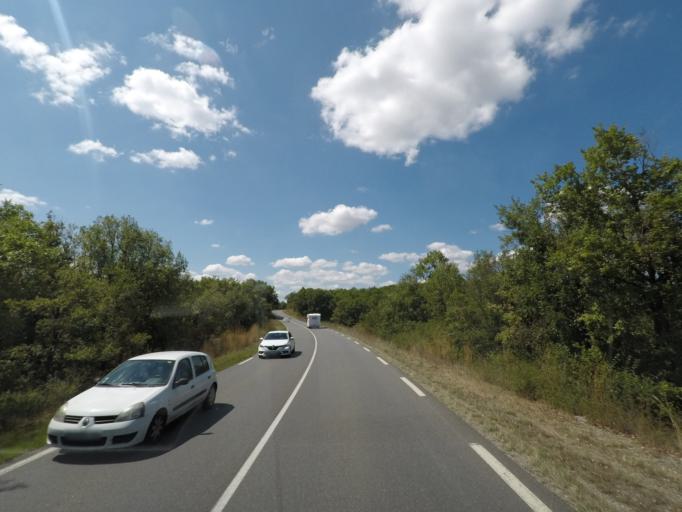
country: FR
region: Midi-Pyrenees
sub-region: Departement du Lot
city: Lacapelle-Marival
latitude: 44.6252
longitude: 1.8975
